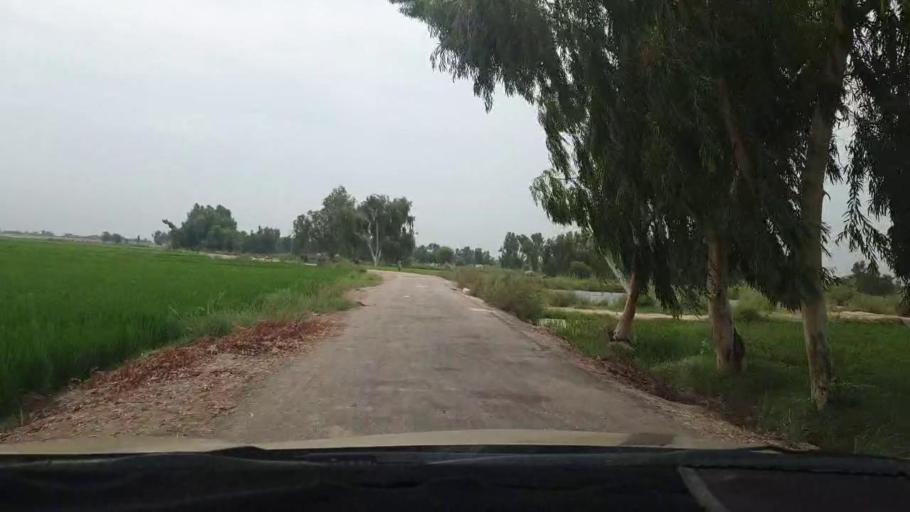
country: PK
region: Sindh
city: Naudero
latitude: 27.6237
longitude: 68.3248
